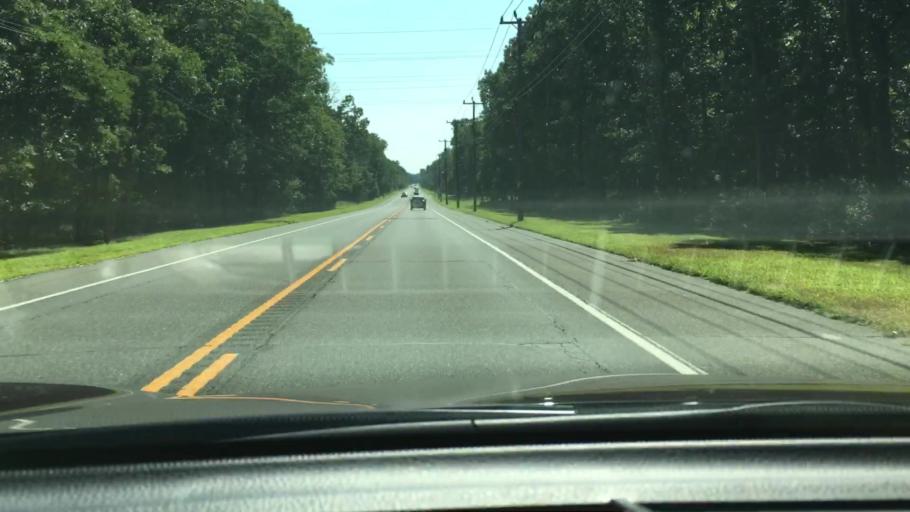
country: US
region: New Jersey
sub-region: Cumberland County
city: Laurel Lake
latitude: 39.3798
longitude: -74.9665
